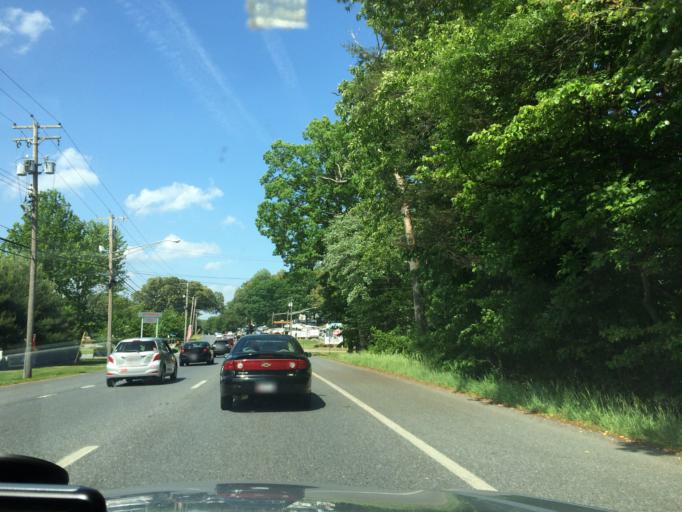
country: US
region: Maryland
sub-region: Anne Arundel County
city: Gambrills
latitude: 39.0484
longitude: -76.6628
